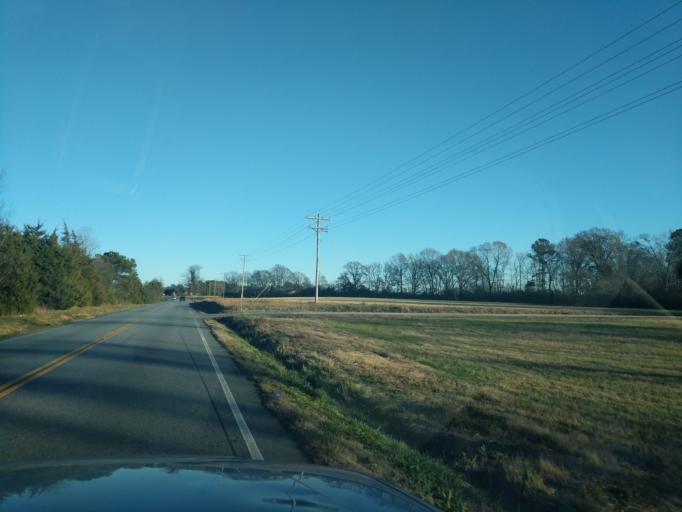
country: US
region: South Carolina
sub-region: Oconee County
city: Seneca
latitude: 34.5938
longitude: -82.9948
